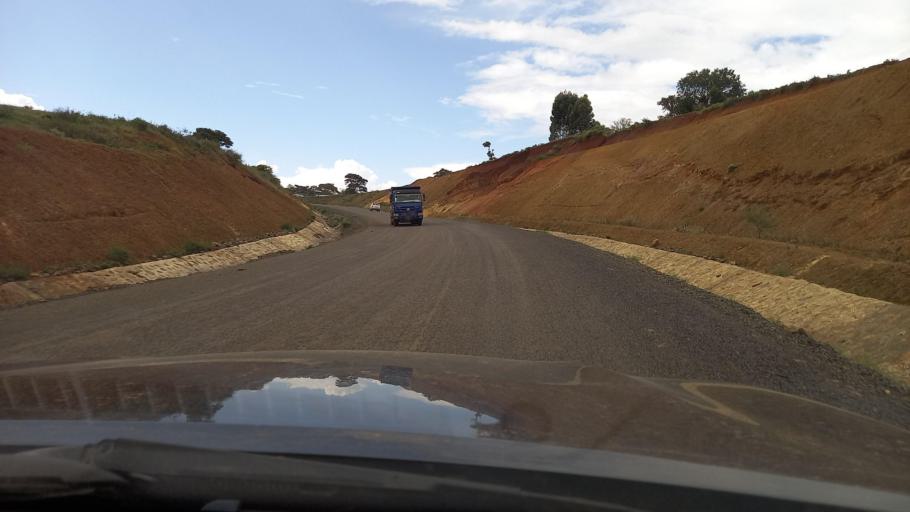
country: ET
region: Southern Nations, Nationalities, and People's Region
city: Mizan Teferi
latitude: 6.2111
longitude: 35.6421
